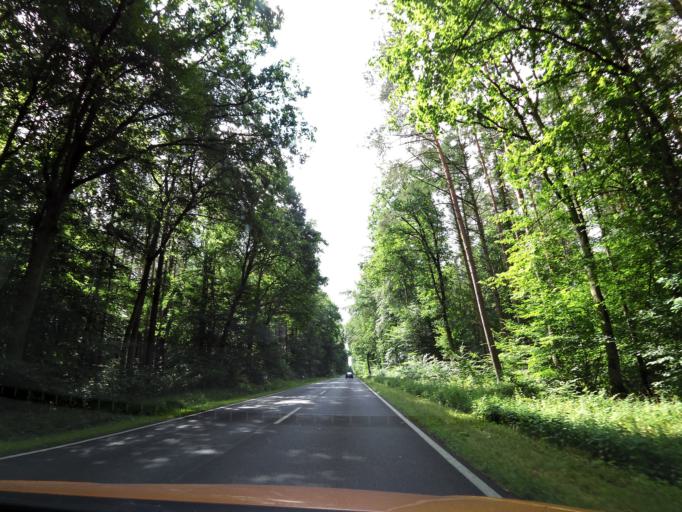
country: DE
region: Mecklenburg-Vorpommern
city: Muhl Rosin
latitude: 53.7547
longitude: 12.2505
